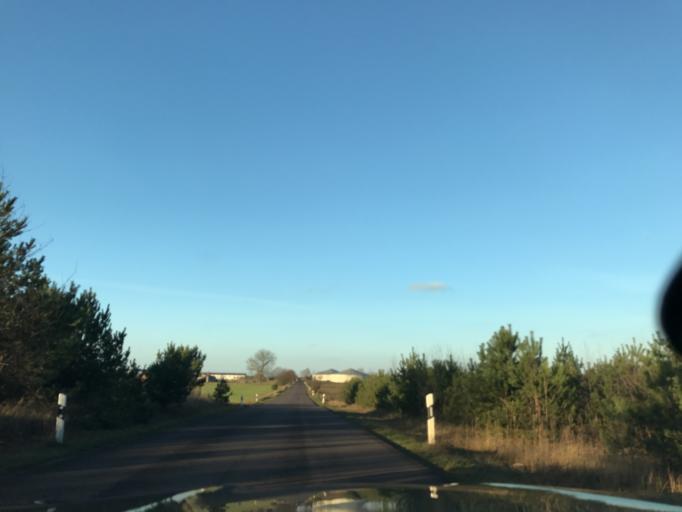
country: DE
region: Saxony-Anhalt
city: Burg bei Magdeburg
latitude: 52.2735
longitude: 11.9440
